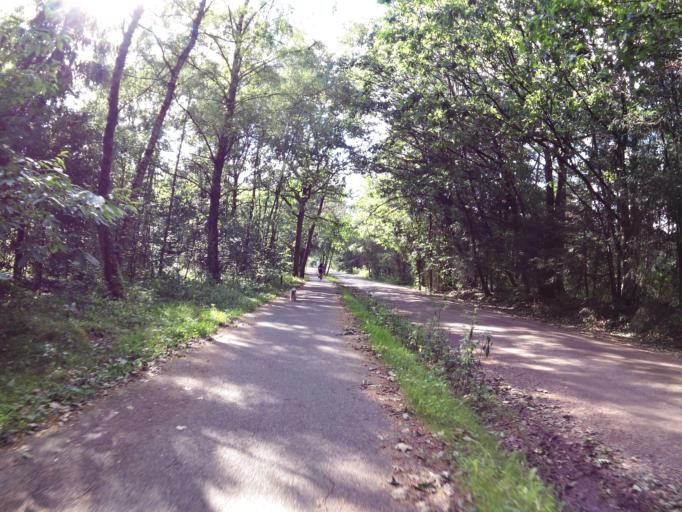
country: NL
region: North Brabant
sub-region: Gemeente Eindhoven
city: Lakerlopen
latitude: 51.3909
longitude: 5.5036
